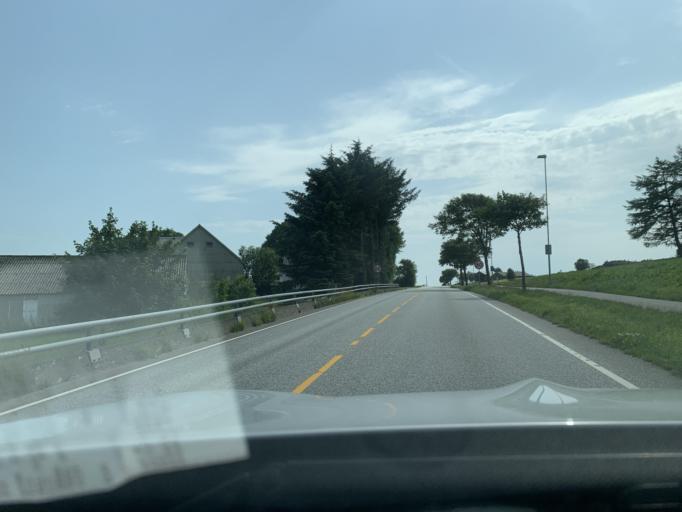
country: NO
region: Rogaland
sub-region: Klepp
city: Kleppe
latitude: 58.7666
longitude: 5.6279
